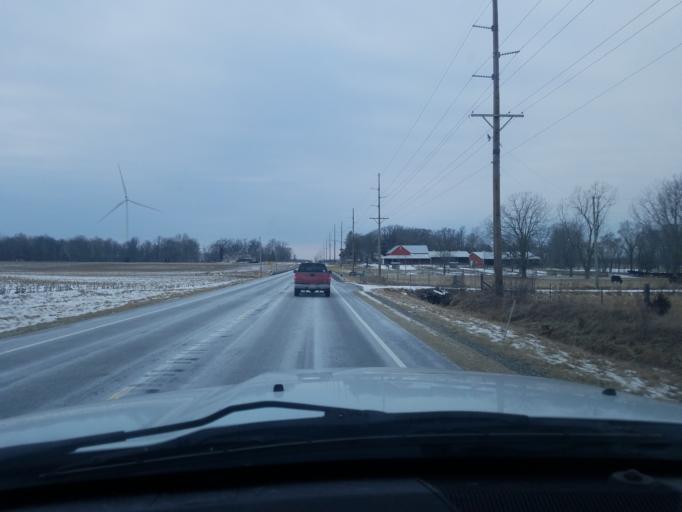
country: US
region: Indiana
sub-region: Randolph County
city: Farmland
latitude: 40.1714
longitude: -85.0597
